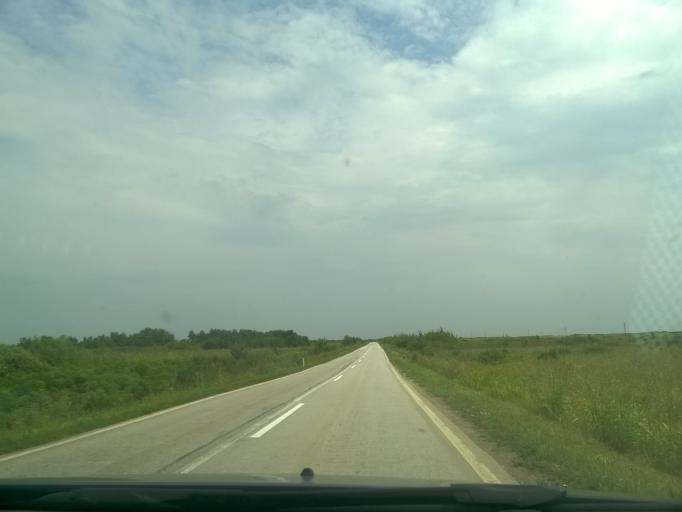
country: RS
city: Boka
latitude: 45.3487
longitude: 20.8004
